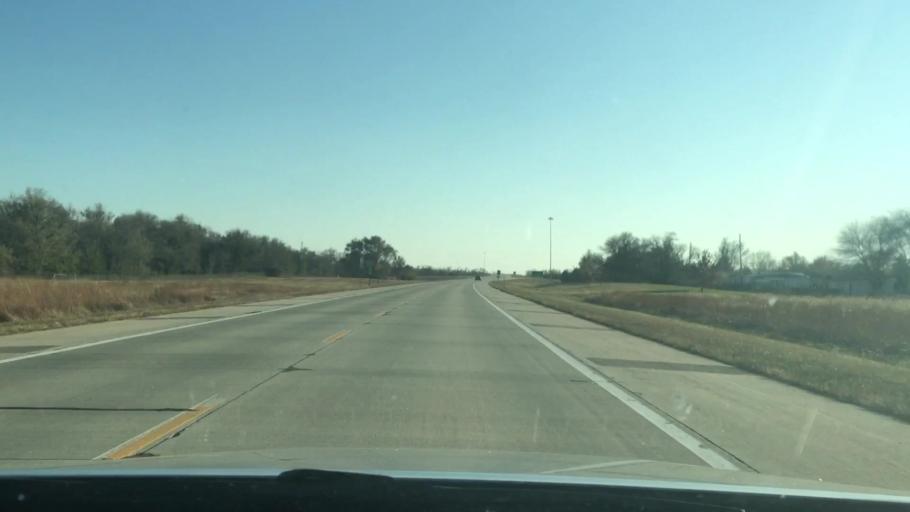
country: US
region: Kansas
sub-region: Reno County
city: Hutchinson
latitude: 38.0652
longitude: -97.9861
